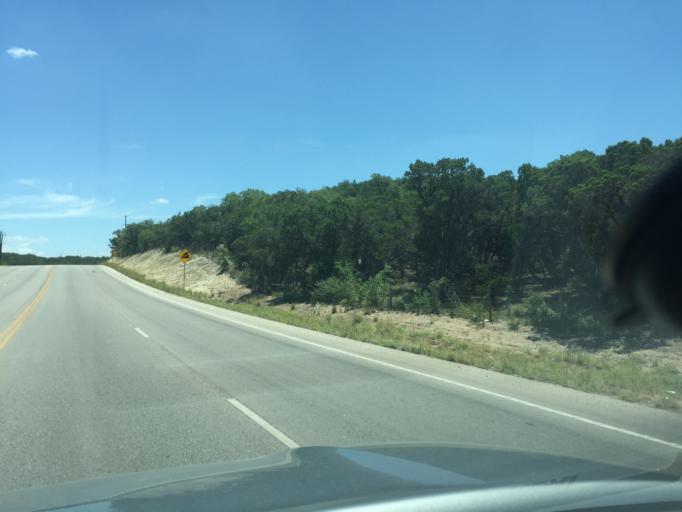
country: US
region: Texas
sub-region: Bexar County
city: Timberwood Park
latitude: 29.7130
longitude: -98.4515
